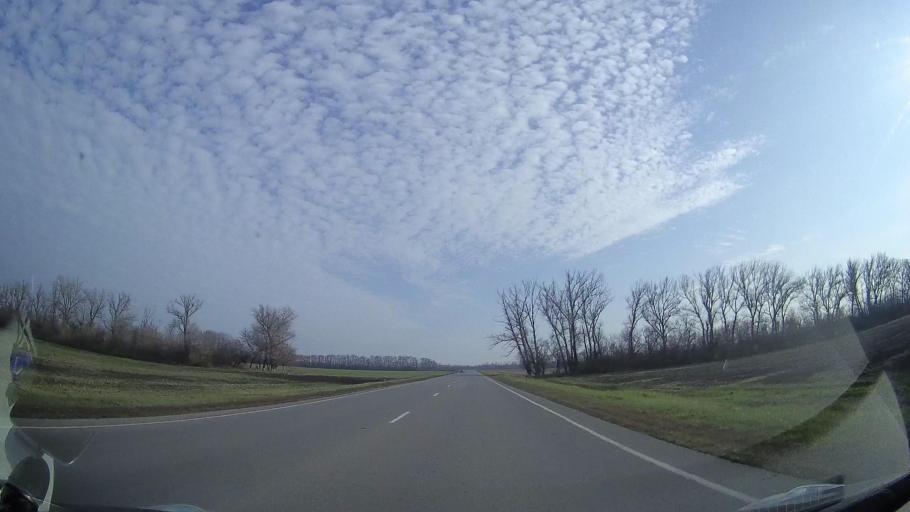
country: RU
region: Rostov
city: Tselina
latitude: 46.5225
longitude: 41.1344
